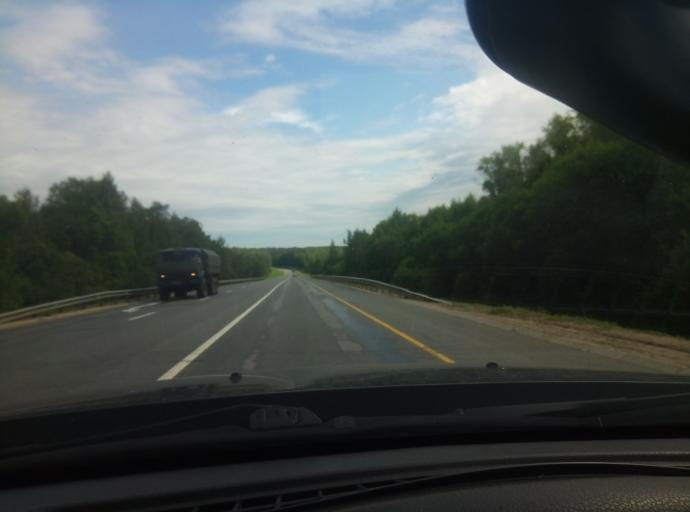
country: RU
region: Tula
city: Barsuki
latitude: 54.3124
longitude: 37.5431
